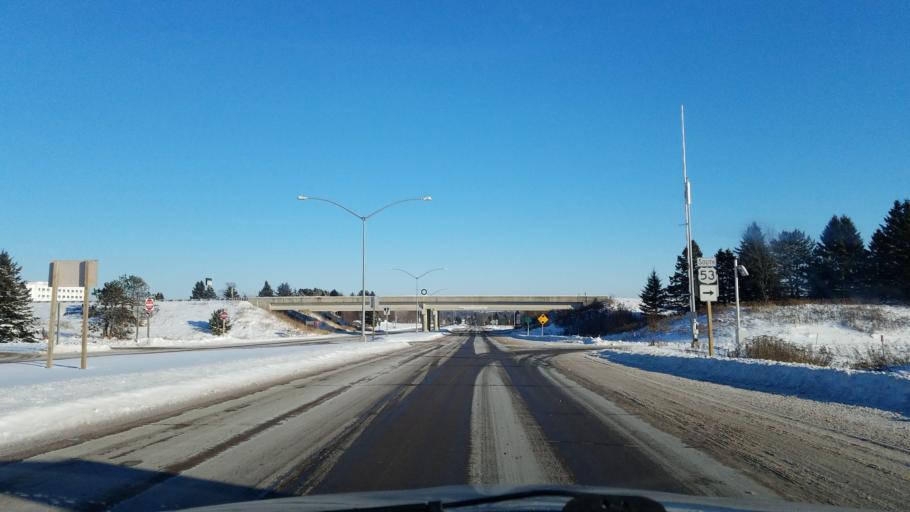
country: US
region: Wisconsin
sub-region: Barron County
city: Rice Lake
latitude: 45.5093
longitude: -91.7640
